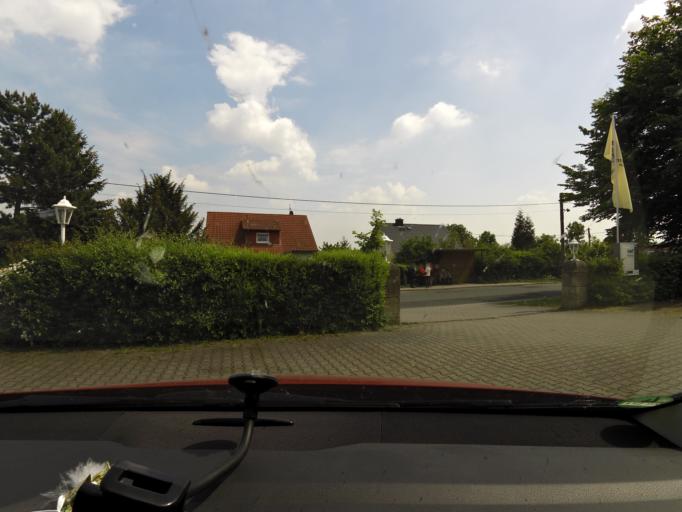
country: DE
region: Thuringia
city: Oberdorla
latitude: 51.2003
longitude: 10.3978
